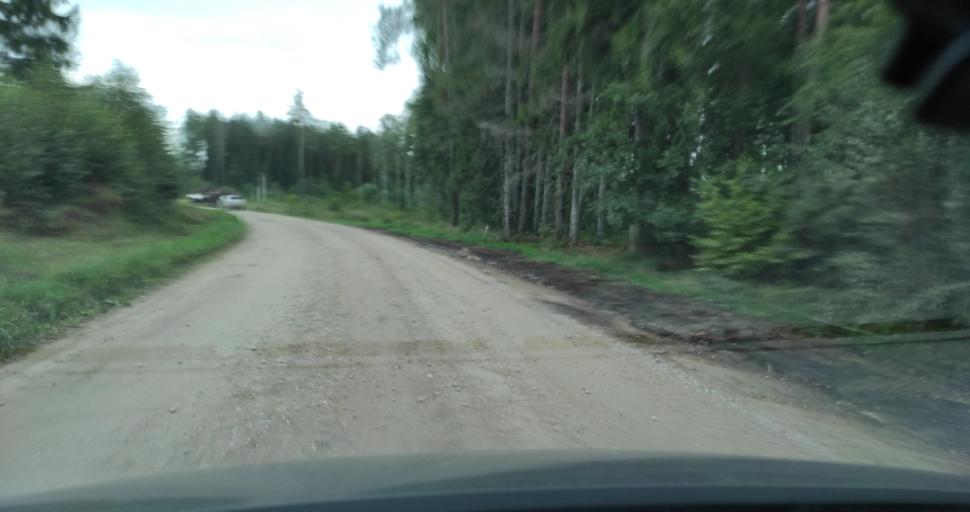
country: LV
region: Talsu Rajons
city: Stende
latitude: 57.0434
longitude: 22.3068
